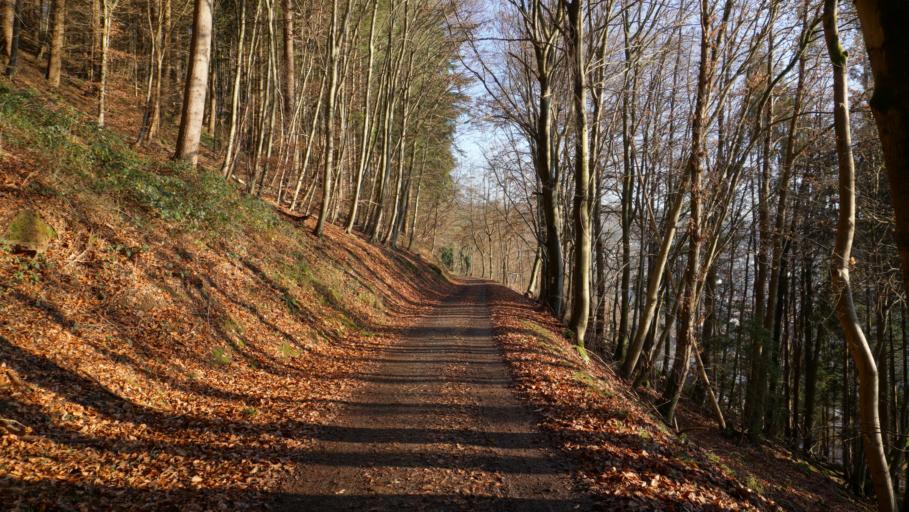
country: DE
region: Baden-Wuerttemberg
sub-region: Karlsruhe Region
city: Neckargerach
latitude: 49.4051
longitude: 9.0640
